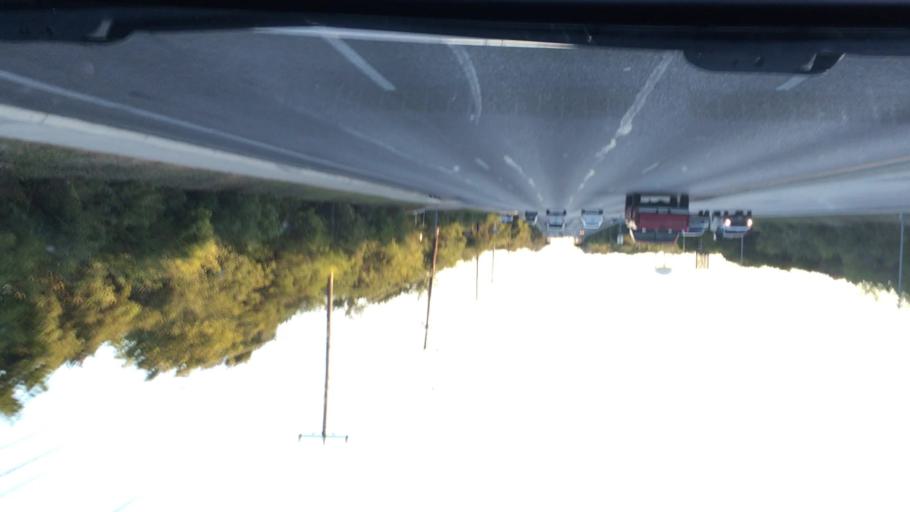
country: US
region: Texas
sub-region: Bexar County
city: Castle Hills
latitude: 29.5532
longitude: -98.5332
